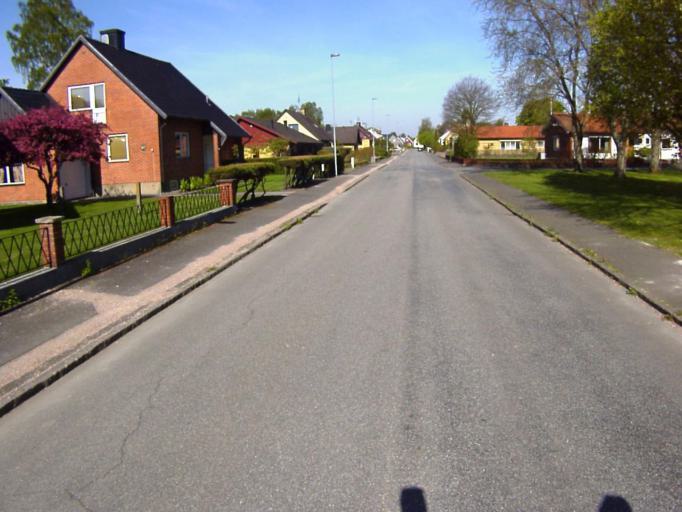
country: SE
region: Skane
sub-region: Kristianstads Kommun
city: Onnestad
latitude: 55.9317
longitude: 13.9707
